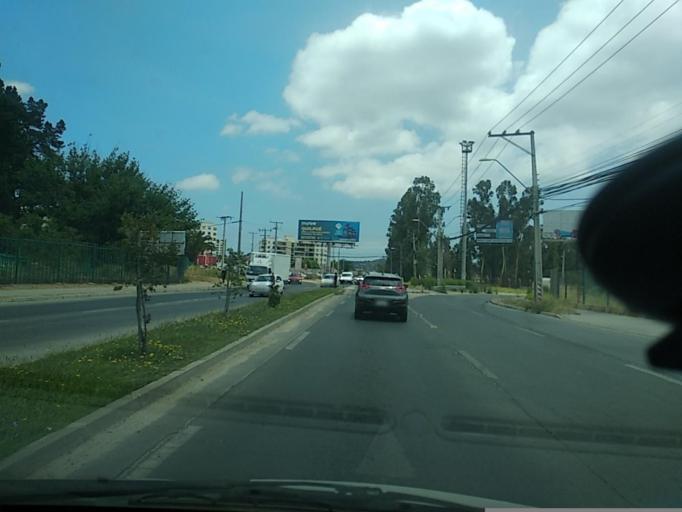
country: CL
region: Valparaiso
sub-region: Provincia de Marga Marga
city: Quilpue
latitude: -33.0431
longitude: -71.4226
